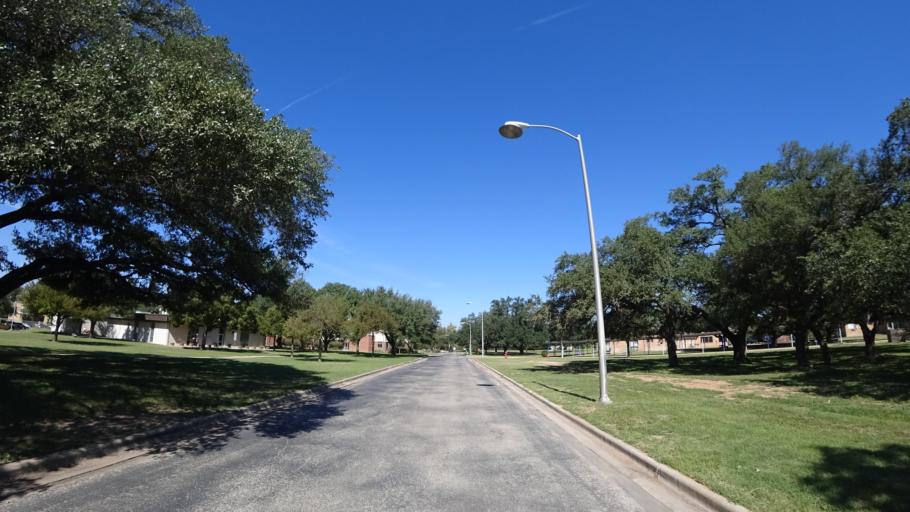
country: US
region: Texas
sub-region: Travis County
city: Hornsby Bend
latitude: 30.2726
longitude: -97.6381
